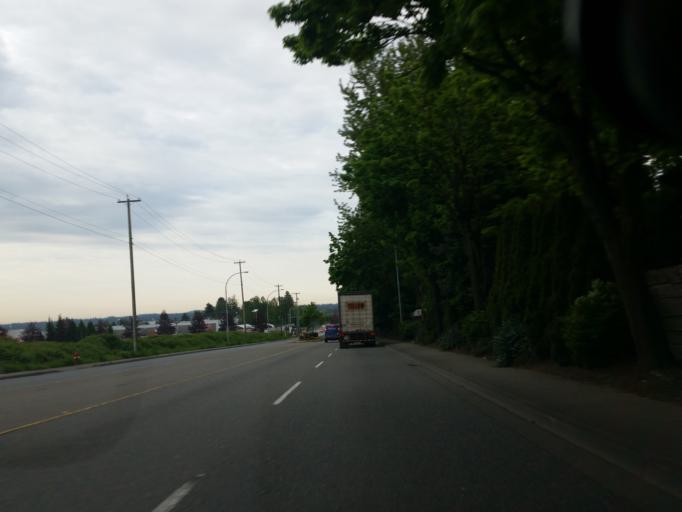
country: CA
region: British Columbia
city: Langley
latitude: 49.1252
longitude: -122.6687
